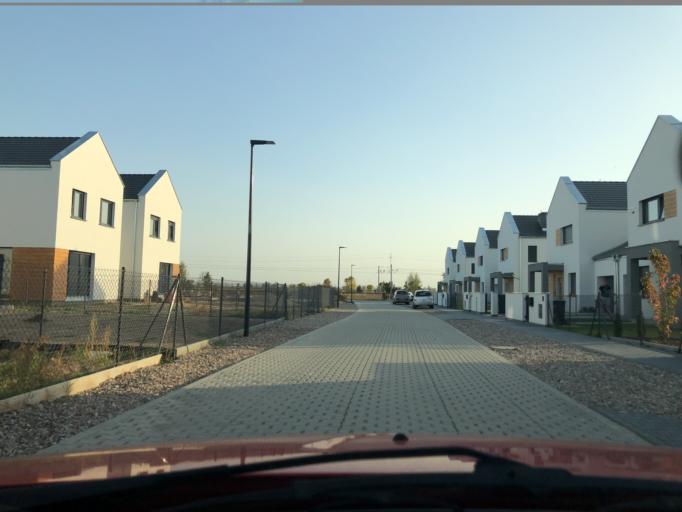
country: PL
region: Greater Poland Voivodeship
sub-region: Powiat poznanski
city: Dopiewo
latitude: 52.3721
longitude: 16.7252
